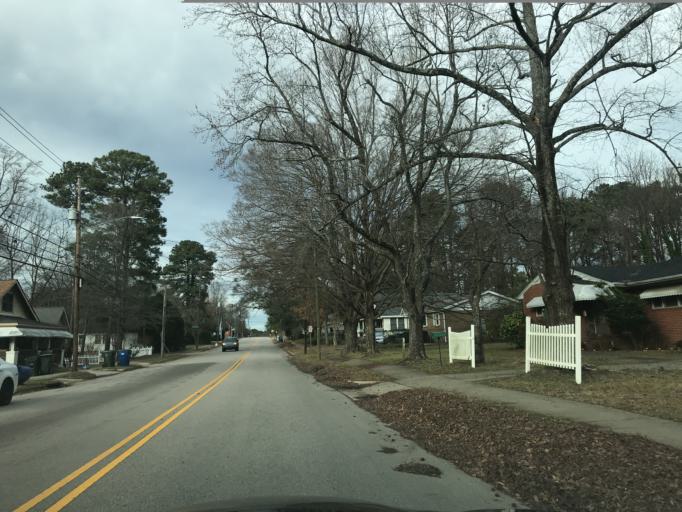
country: US
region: North Carolina
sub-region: Wake County
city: West Raleigh
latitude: 35.7902
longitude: -78.6938
